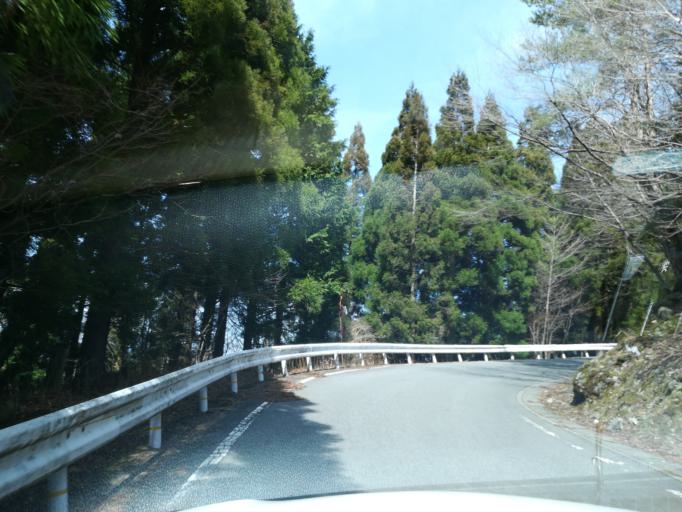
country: JP
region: Tokushima
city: Wakimachi
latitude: 33.8784
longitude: 134.0539
